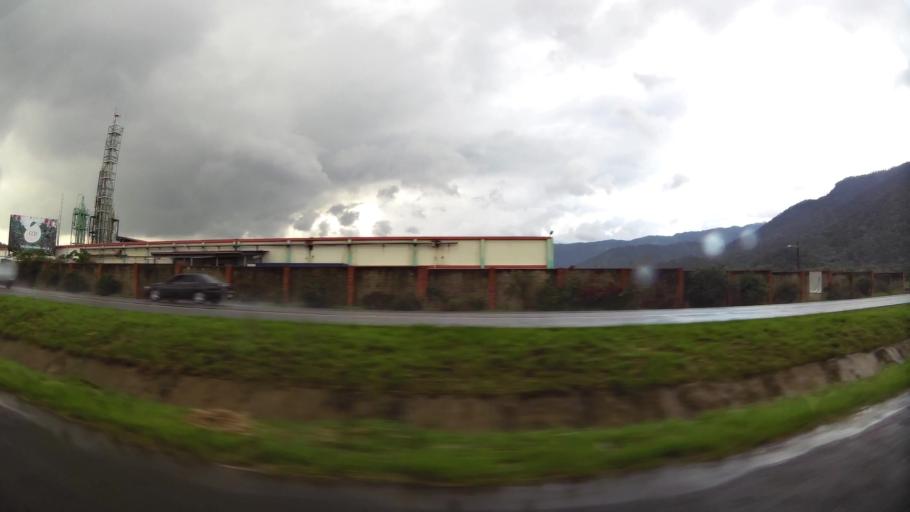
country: DO
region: San Cristobal
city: Villa Altagracia
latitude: 18.7086
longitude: -70.2039
